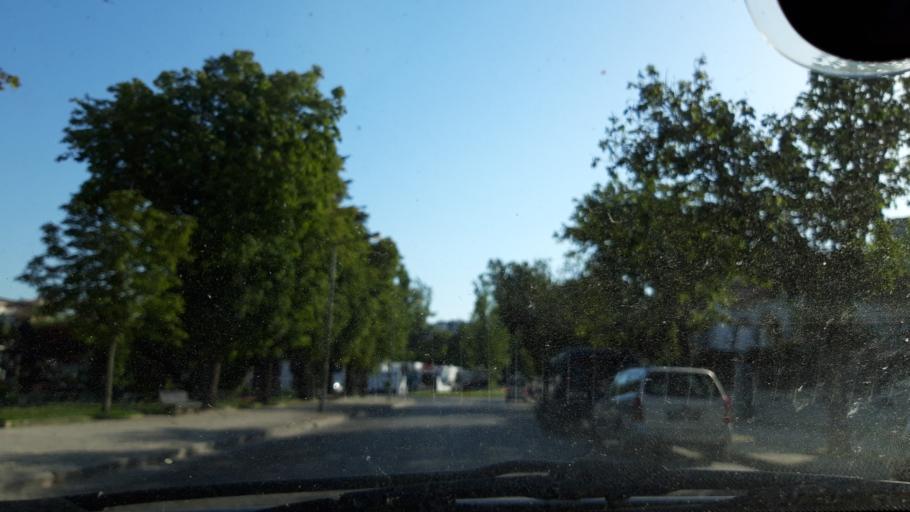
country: PT
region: Santarem
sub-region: Torres Novas
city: Torres Novas
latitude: 39.4812
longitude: -8.5412
